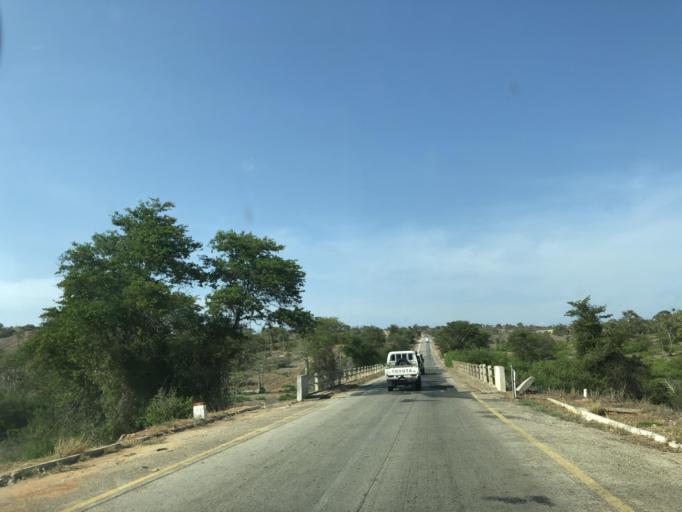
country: AO
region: Luanda
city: Luanda
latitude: -9.5445
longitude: 13.2148
